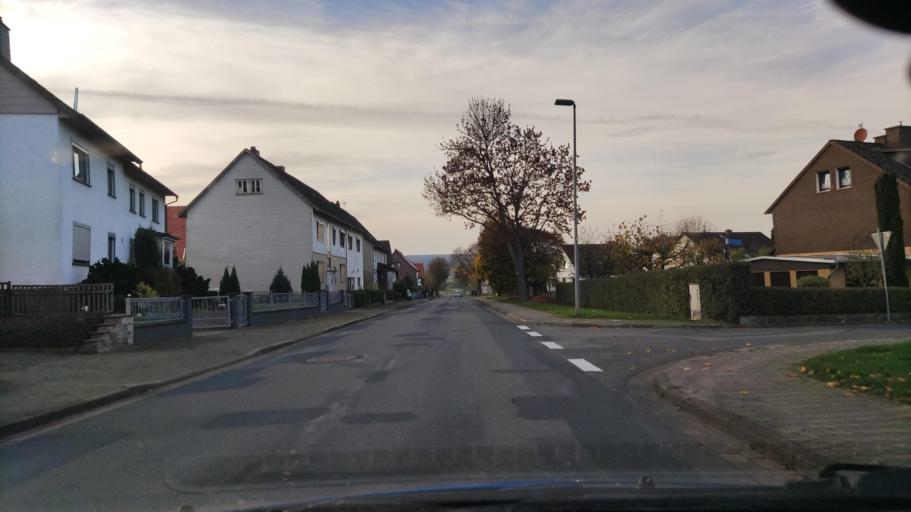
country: DE
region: Lower Saxony
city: Dassel
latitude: 51.7732
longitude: 9.7161
